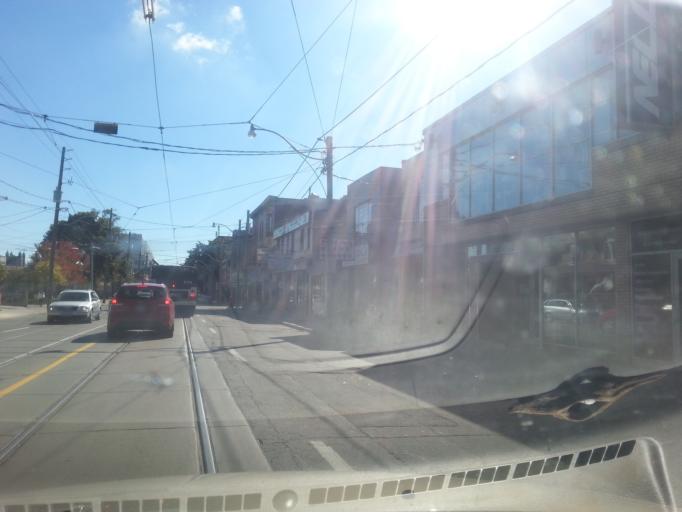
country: CA
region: Ontario
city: Toronto
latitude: 43.6673
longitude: -79.4121
